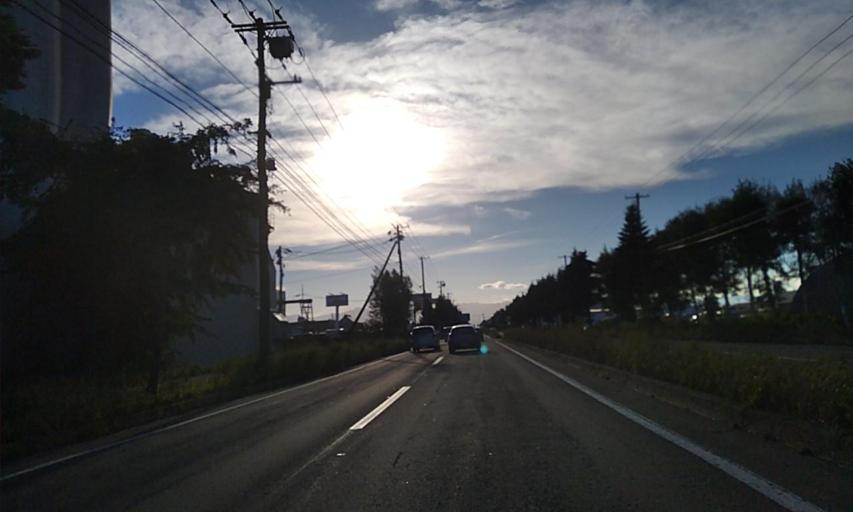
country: JP
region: Hokkaido
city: Obihiro
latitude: 42.9271
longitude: 143.1336
